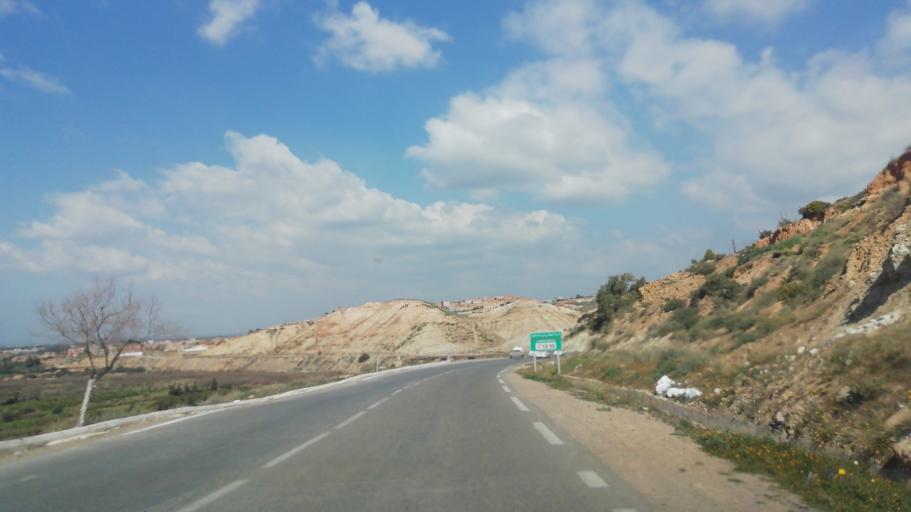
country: DZ
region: Mascara
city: Mascara
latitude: 35.5605
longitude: 0.0692
